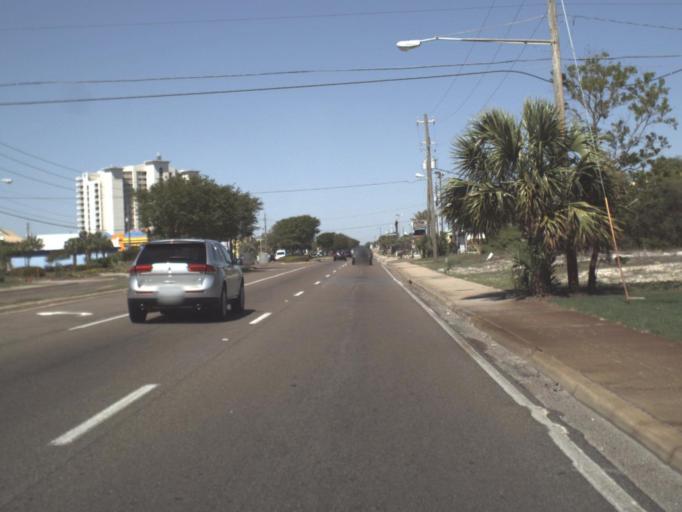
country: US
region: Florida
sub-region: Okaloosa County
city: Destin
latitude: 30.3869
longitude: -86.4706
